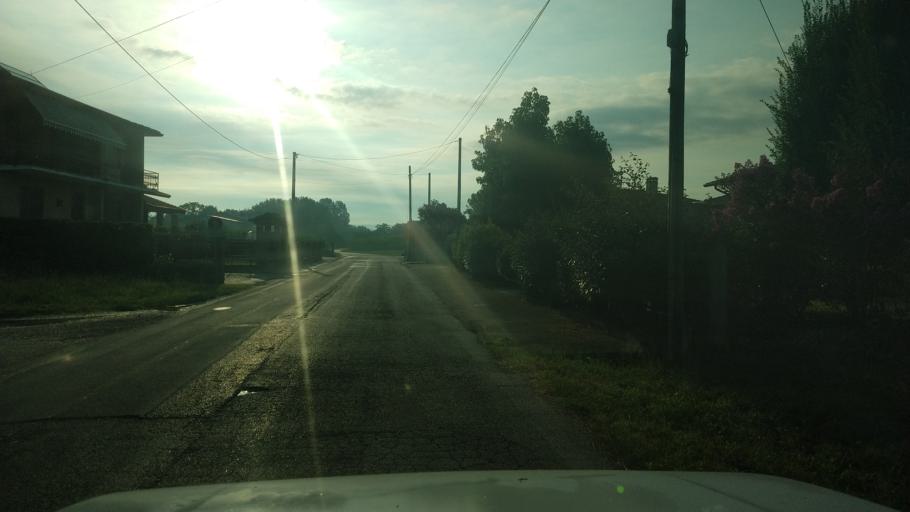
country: IT
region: Veneto
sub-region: Provincia di Vicenza
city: Nove
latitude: 45.7195
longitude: 11.6543
